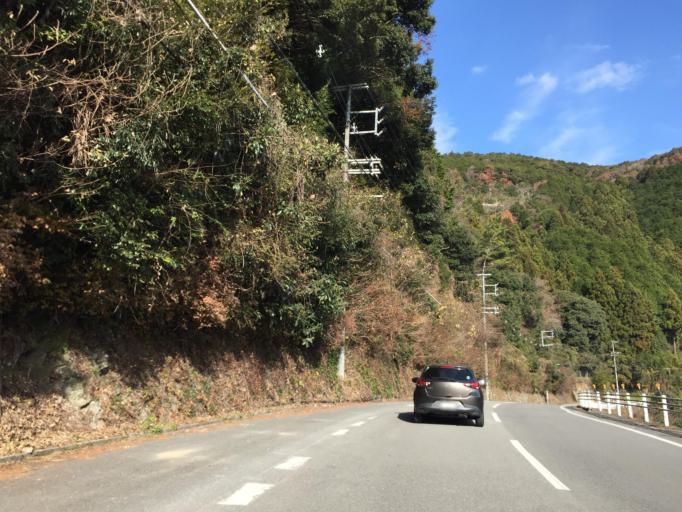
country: JP
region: Wakayama
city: Iwade
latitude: 34.1397
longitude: 135.4090
